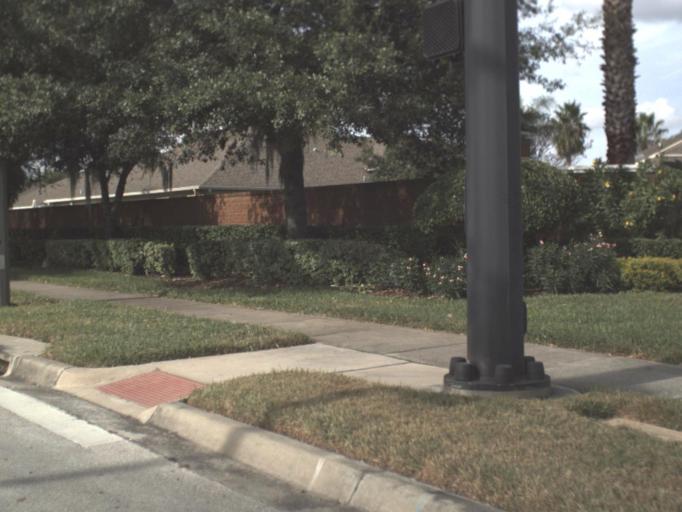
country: US
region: Florida
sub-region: Orange County
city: Conway
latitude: 28.4237
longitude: -81.2497
